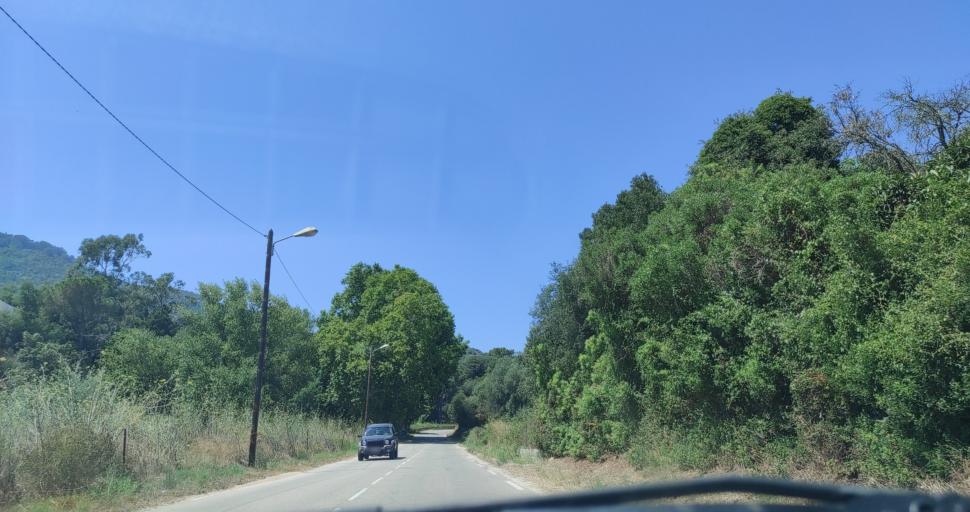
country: FR
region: Corsica
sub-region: Departement de la Corse-du-Sud
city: Ajaccio
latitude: 41.9509
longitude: 8.7336
